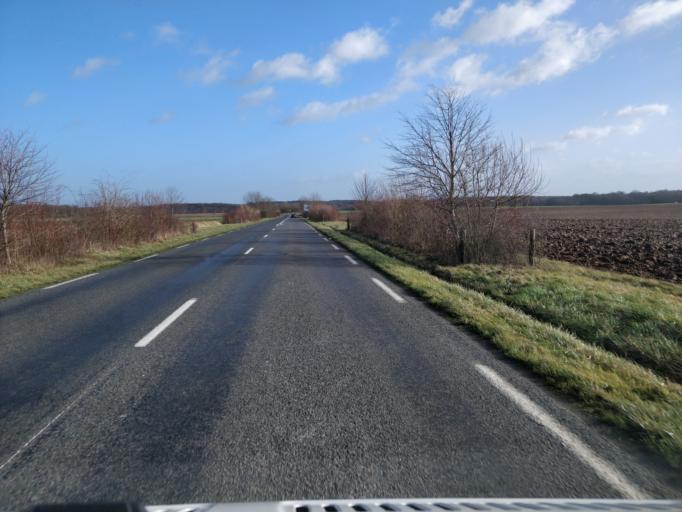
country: FR
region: Ile-de-France
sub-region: Departement de Seine-et-Marne
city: Lorrez-le-Bocage-Preaux
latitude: 48.2195
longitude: 2.8878
